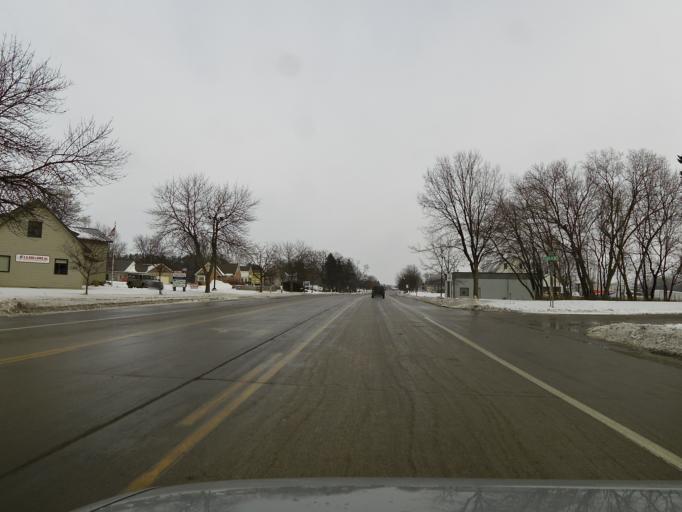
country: US
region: Minnesota
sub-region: McLeod County
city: Hutchinson
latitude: 44.8954
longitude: -94.3597
